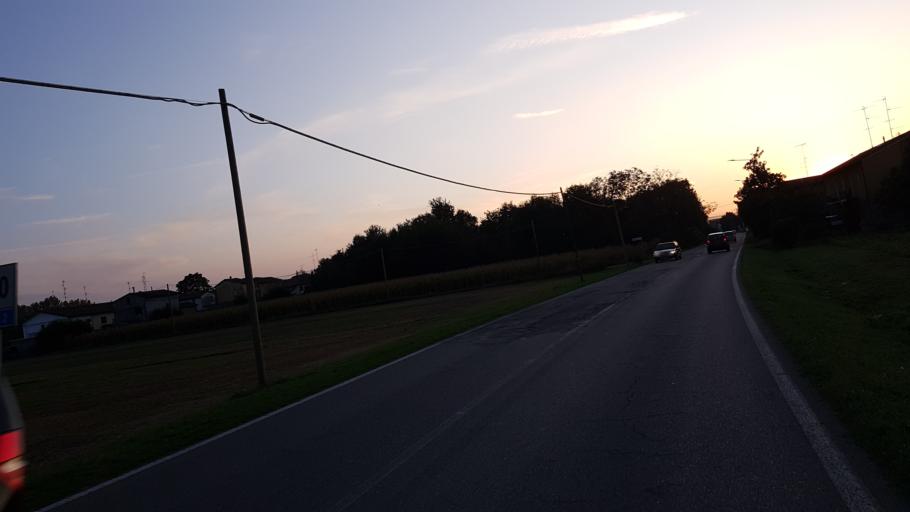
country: IT
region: Emilia-Romagna
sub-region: Provincia di Modena
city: Camposanto
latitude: 44.7883
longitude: 11.1525
